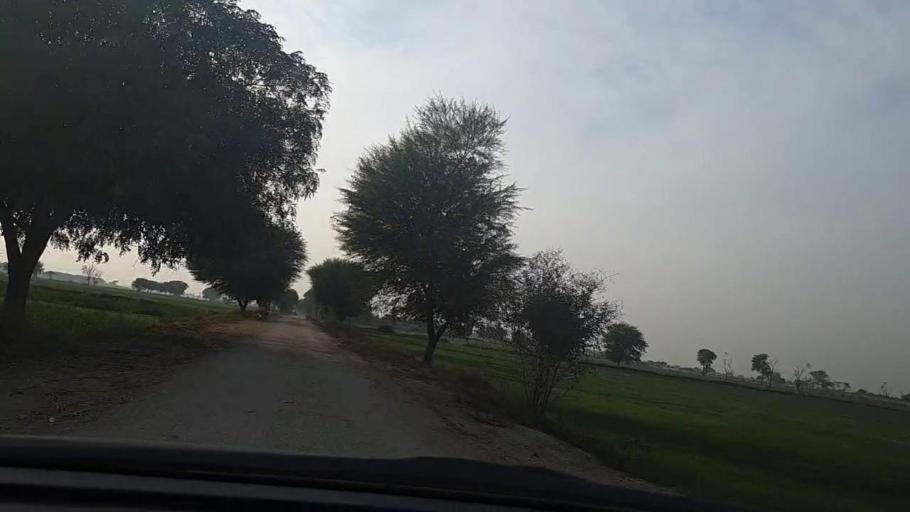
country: PK
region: Sindh
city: Daulatpur
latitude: 26.3369
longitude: 68.0296
